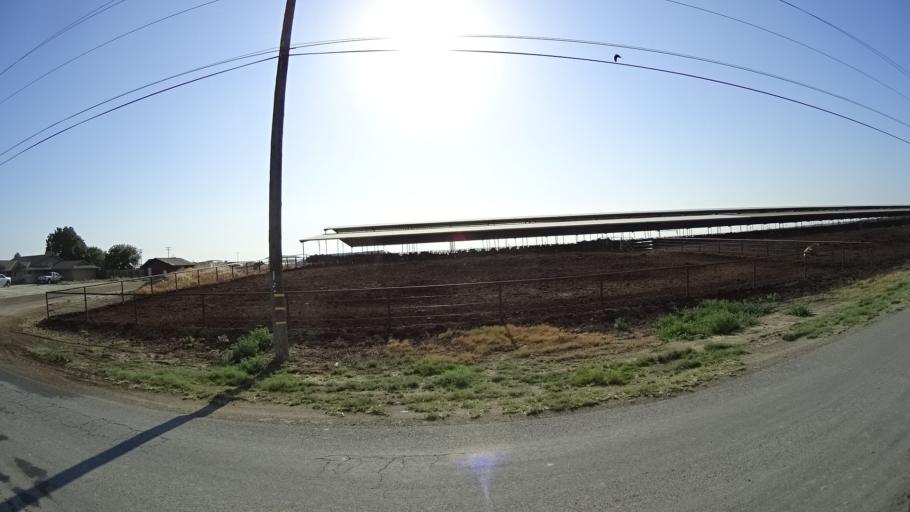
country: US
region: California
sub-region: Kings County
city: Home Garden
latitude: 36.3237
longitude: -119.5651
